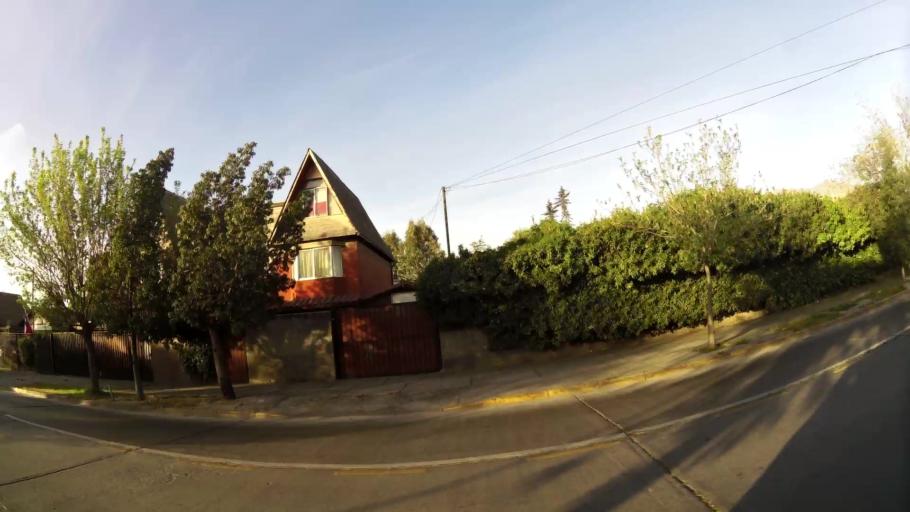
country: CL
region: Santiago Metropolitan
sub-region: Provincia de Cordillera
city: Puente Alto
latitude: -33.5528
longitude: -70.5815
